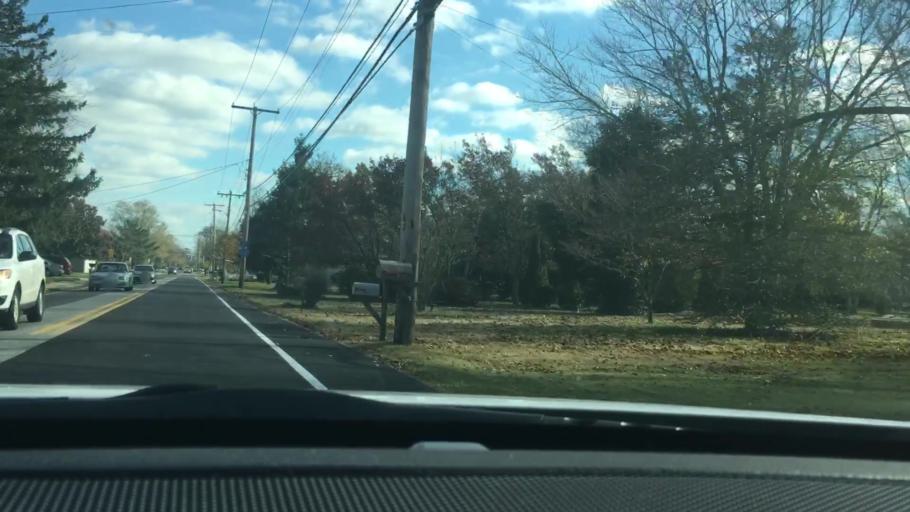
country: US
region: New Jersey
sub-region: Atlantic County
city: Northfield
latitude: 39.3710
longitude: -74.5631
